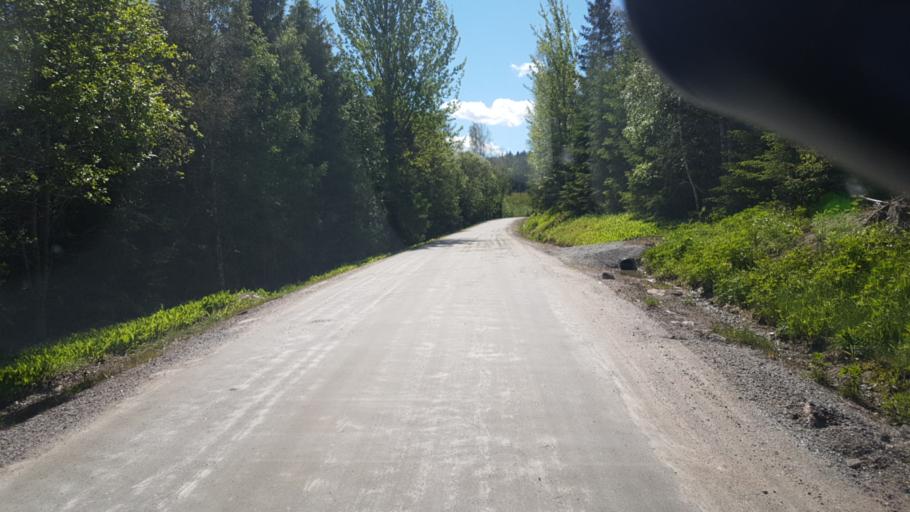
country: SE
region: Vaermland
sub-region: Arvika Kommun
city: Arvika
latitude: 59.6614
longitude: 12.7606
